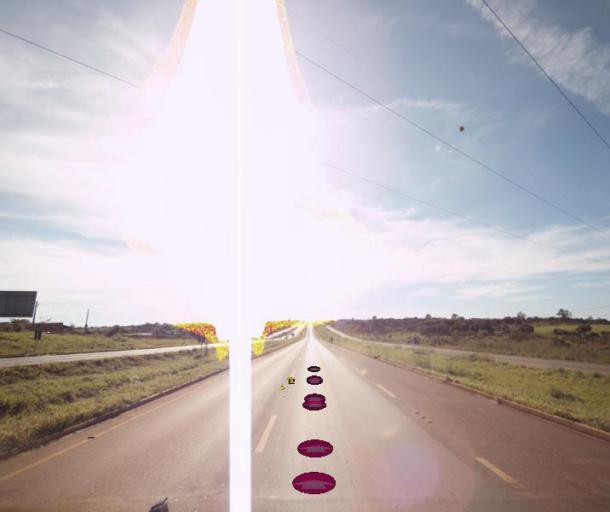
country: BR
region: Federal District
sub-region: Brasilia
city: Brasilia
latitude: -15.7406
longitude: -48.3105
